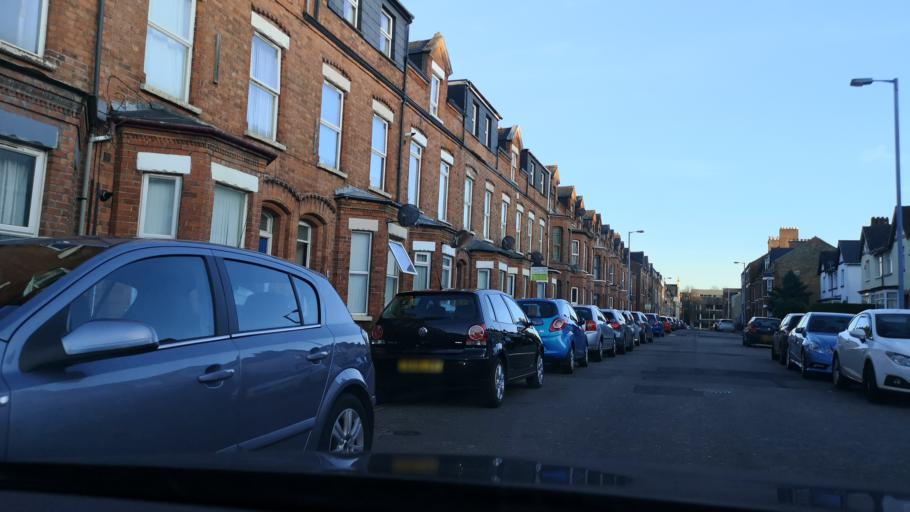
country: GB
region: Northern Ireland
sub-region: City of Belfast
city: Belfast
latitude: 54.5831
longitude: -5.9414
